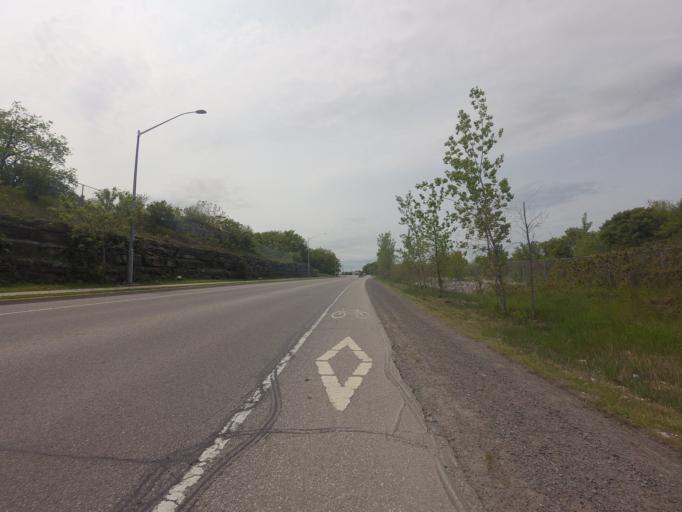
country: CA
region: Ontario
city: Kingston
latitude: 44.2583
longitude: -76.4944
